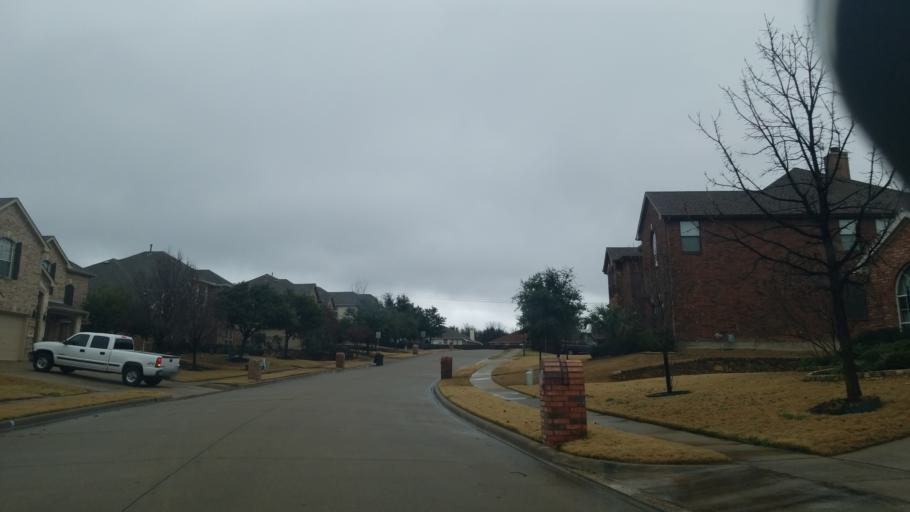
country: US
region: Texas
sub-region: Denton County
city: Corinth
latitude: 33.1394
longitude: -97.0894
